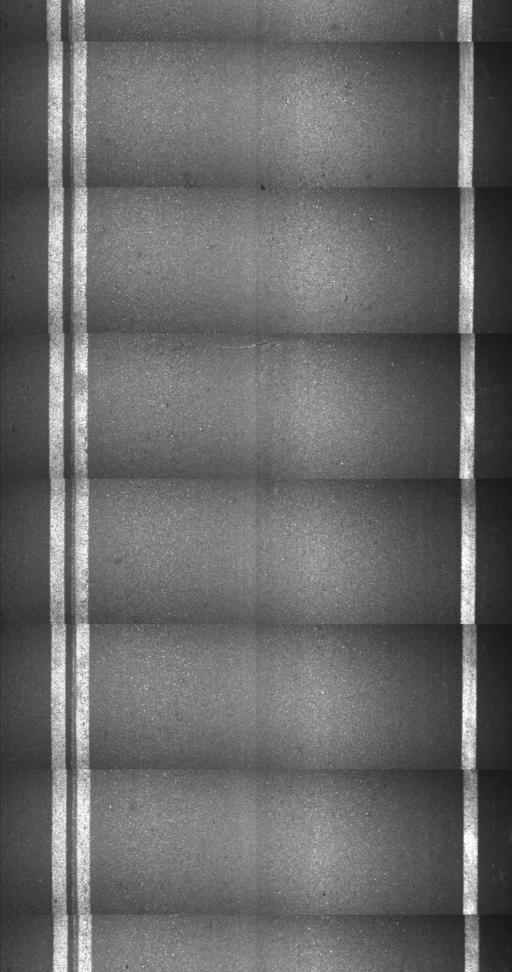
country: US
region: New Hampshire
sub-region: Coos County
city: Colebrook
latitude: 44.9254
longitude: -71.5223
